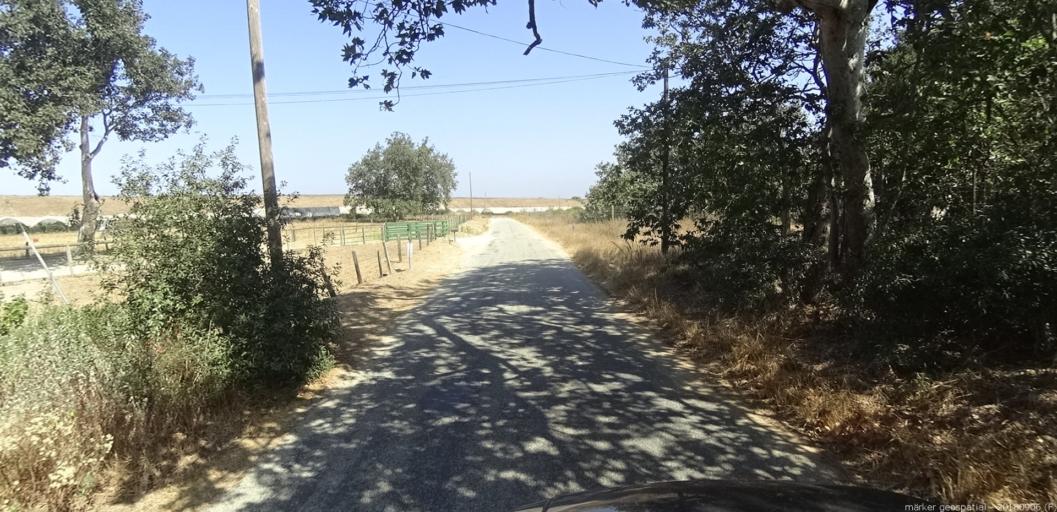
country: US
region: California
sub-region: Monterey County
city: Chualar
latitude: 36.5834
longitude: -121.6071
